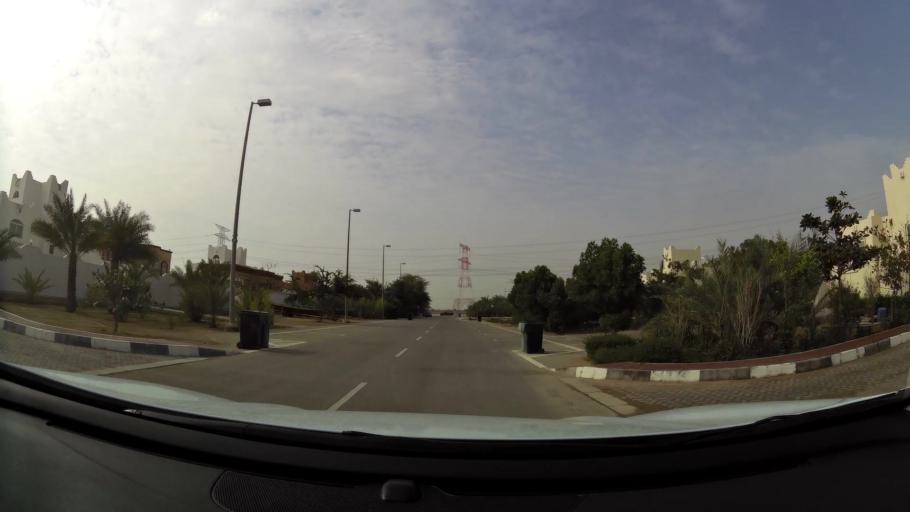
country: AE
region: Abu Dhabi
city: Abu Dhabi
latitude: 24.6556
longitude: 54.7559
